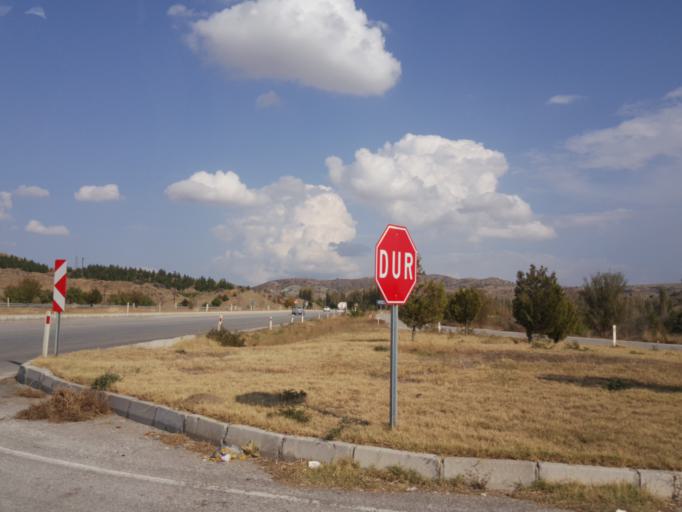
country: TR
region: Corum
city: Sungurlu
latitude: 40.1828
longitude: 34.4865
